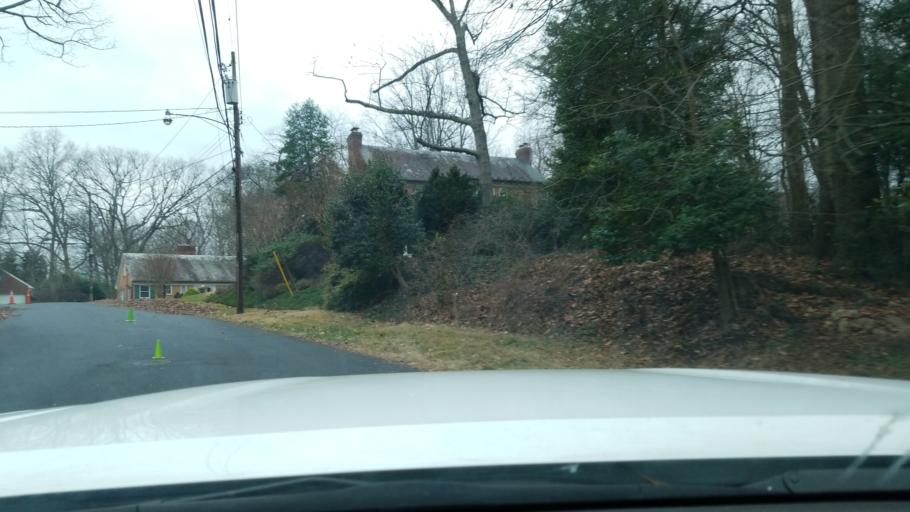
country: US
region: Maryland
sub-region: Montgomery County
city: Chevy Chase
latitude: 38.9415
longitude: -77.0470
